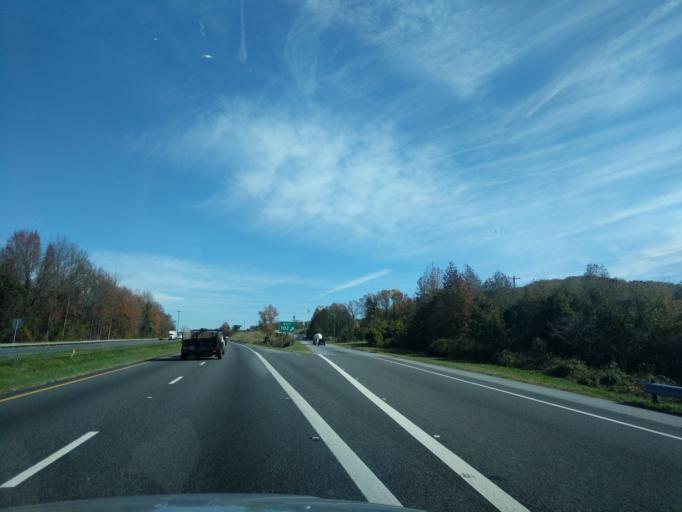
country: US
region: South Carolina
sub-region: Cherokee County
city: Blacksburg
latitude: 35.1373
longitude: -81.5168
